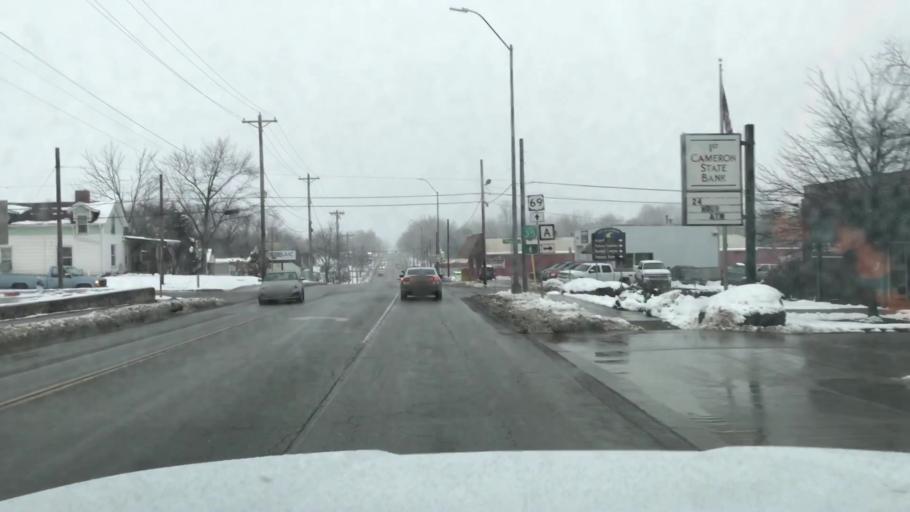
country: US
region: Missouri
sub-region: Clinton County
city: Cameron
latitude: 39.7394
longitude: -94.2360
